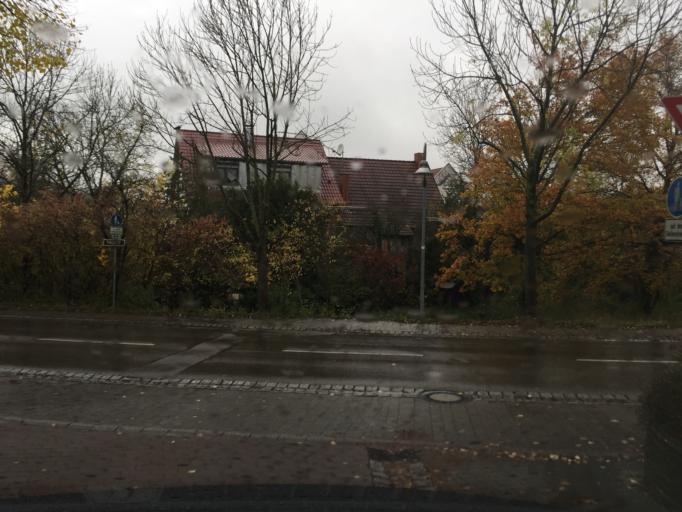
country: DE
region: Baden-Wuerttemberg
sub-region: Regierungsbezirk Stuttgart
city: Eislingen
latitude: 48.6868
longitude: 9.6903
